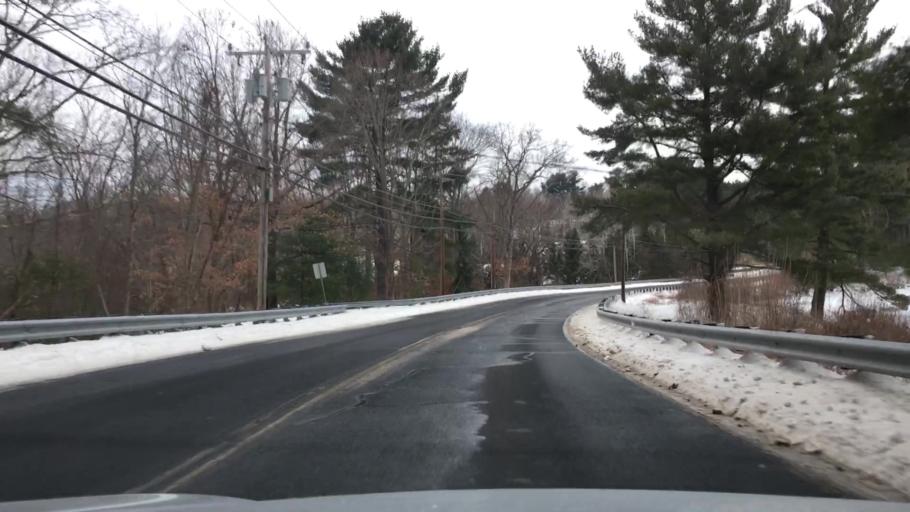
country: US
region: Massachusetts
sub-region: Hampden County
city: Longmeadow
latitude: 42.0419
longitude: -72.5711
